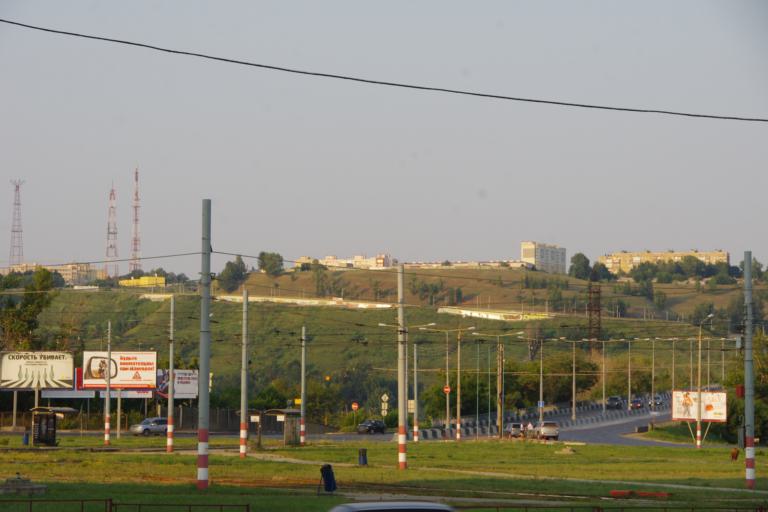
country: RU
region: Nizjnij Novgorod
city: Nizhniy Novgorod
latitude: 56.2983
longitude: 43.9429
